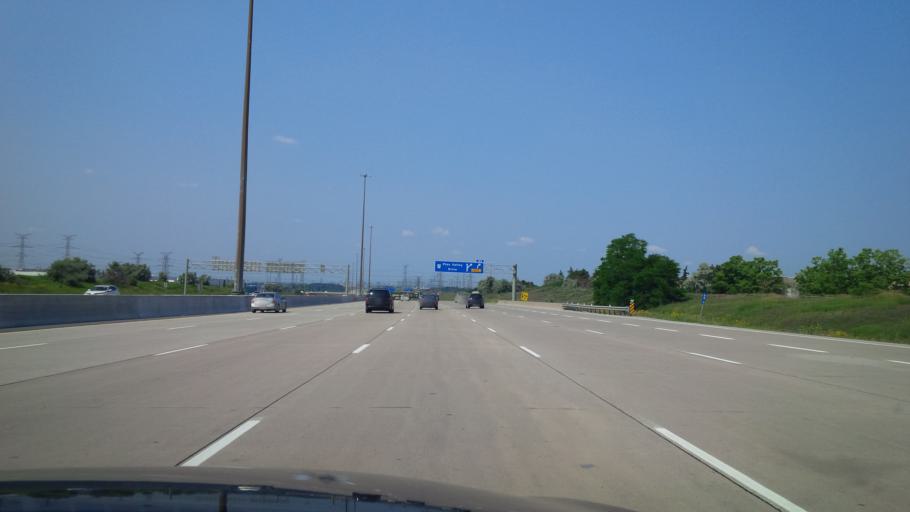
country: CA
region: Ontario
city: Concord
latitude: 43.7784
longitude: -79.5593
